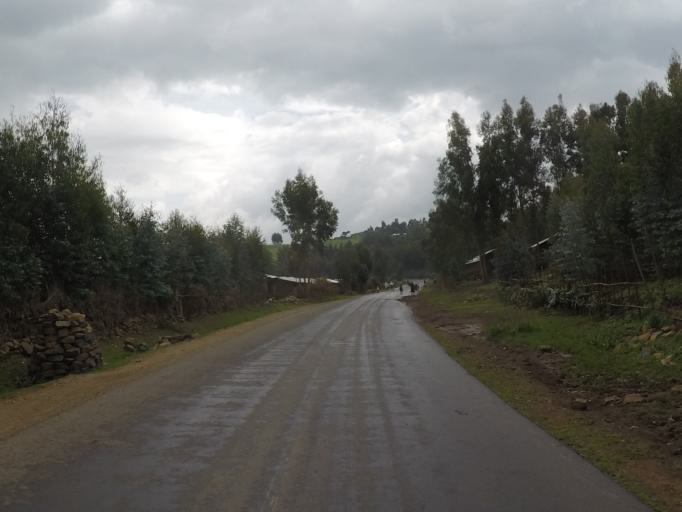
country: ET
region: Amhara
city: Dabat
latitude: 13.0614
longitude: 37.8227
